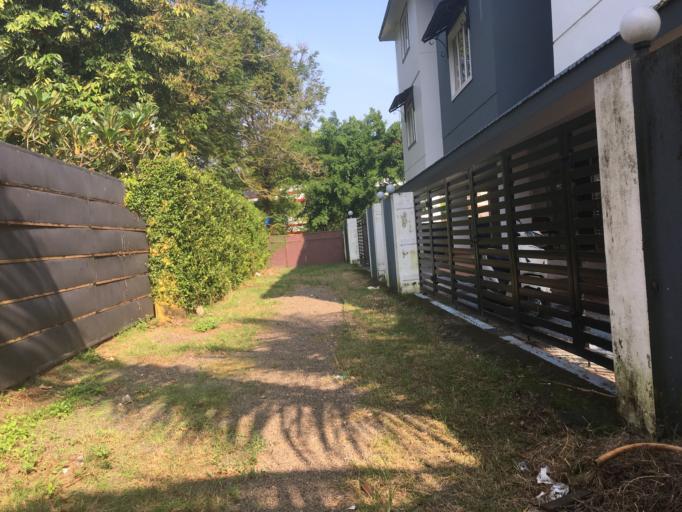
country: IN
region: Kerala
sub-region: Ernakulam
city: Cochin
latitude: 9.9603
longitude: 76.2387
